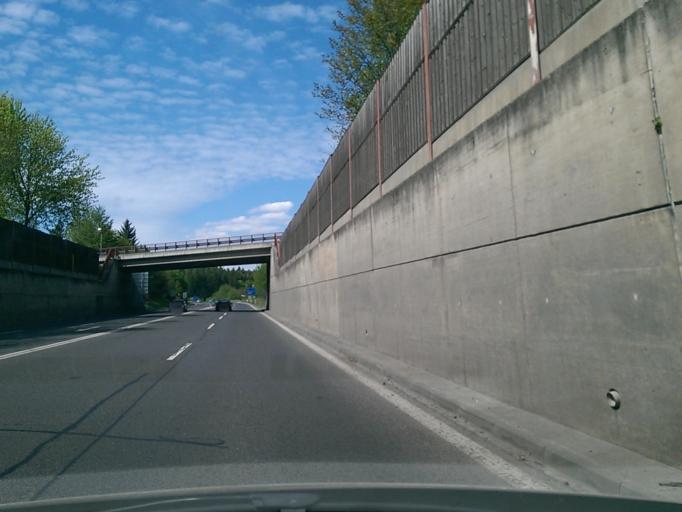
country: CZ
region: Liberecky
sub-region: Okres Semily
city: Turnov
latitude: 50.5898
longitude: 15.1437
